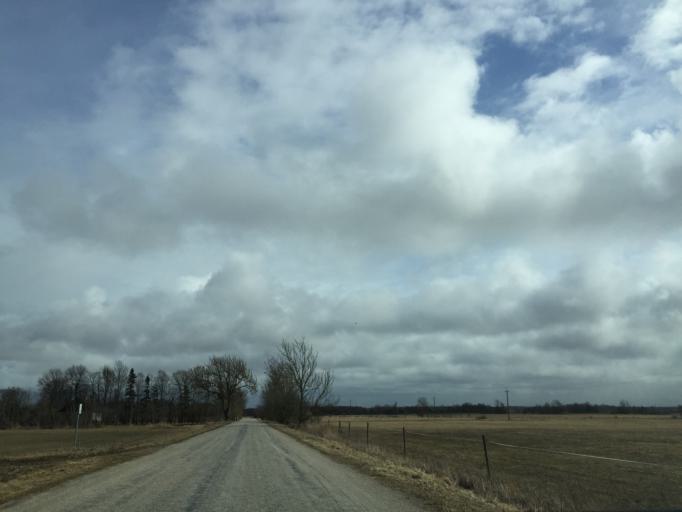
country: EE
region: Laeaene
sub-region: Lihula vald
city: Lihula
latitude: 58.7353
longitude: 23.8428
